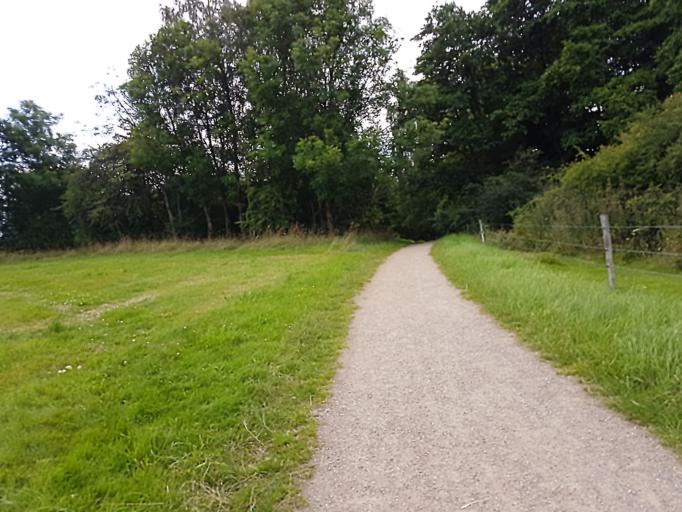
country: DK
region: Capital Region
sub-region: Fureso Kommune
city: Farum
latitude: 55.7954
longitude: 12.3613
